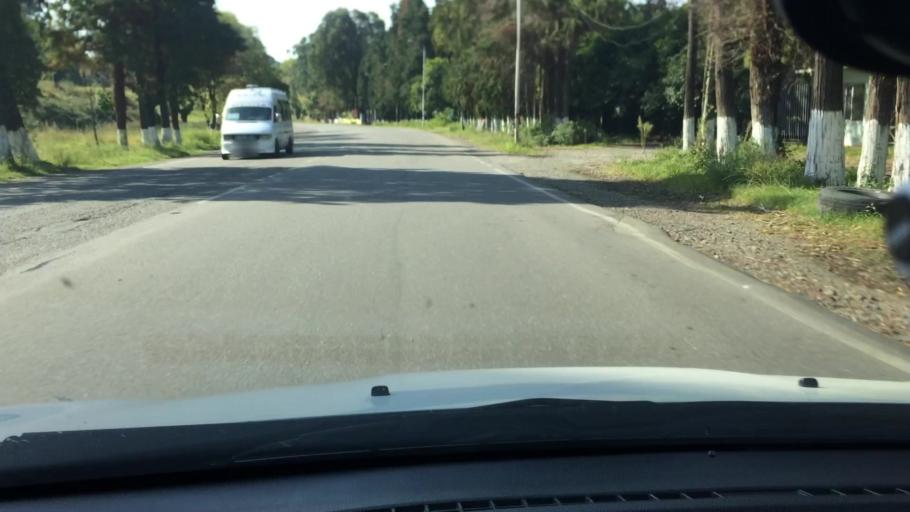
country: GE
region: Ajaria
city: Kobuleti
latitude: 41.7746
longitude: 41.7583
